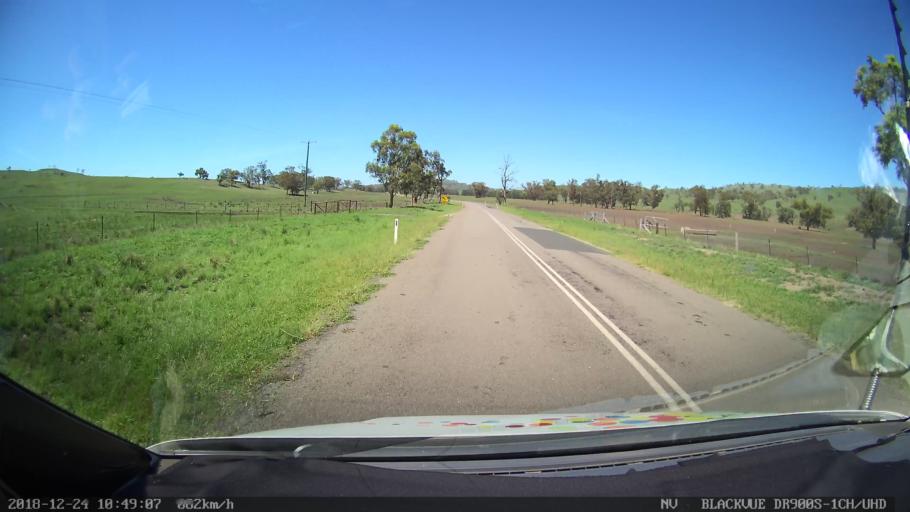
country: AU
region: New South Wales
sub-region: Upper Hunter Shire
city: Merriwa
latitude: -31.9436
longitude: 150.4292
